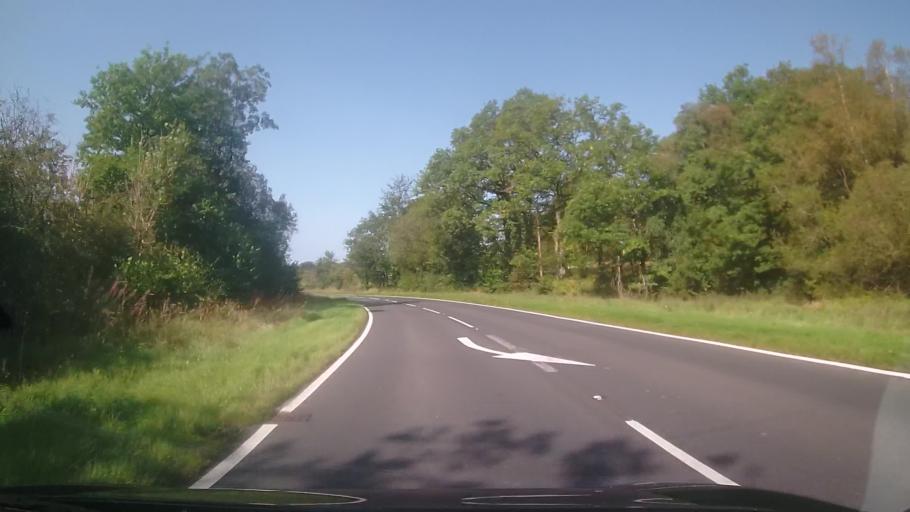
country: GB
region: Wales
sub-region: Sir Powys
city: Builth Wells
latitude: 52.1393
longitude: -3.5510
